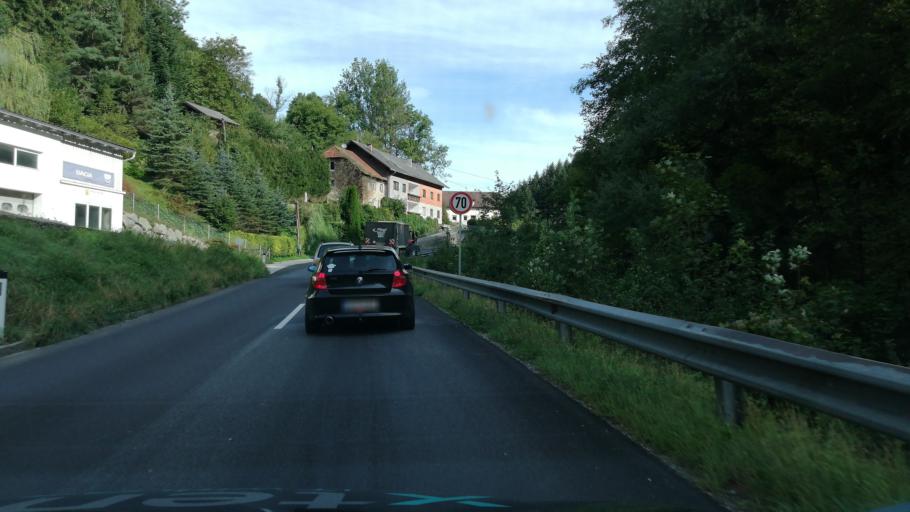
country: AT
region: Lower Austria
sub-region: Politischer Bezirk Amstetten
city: Behamberg
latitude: 47.9998
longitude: 14.4929
